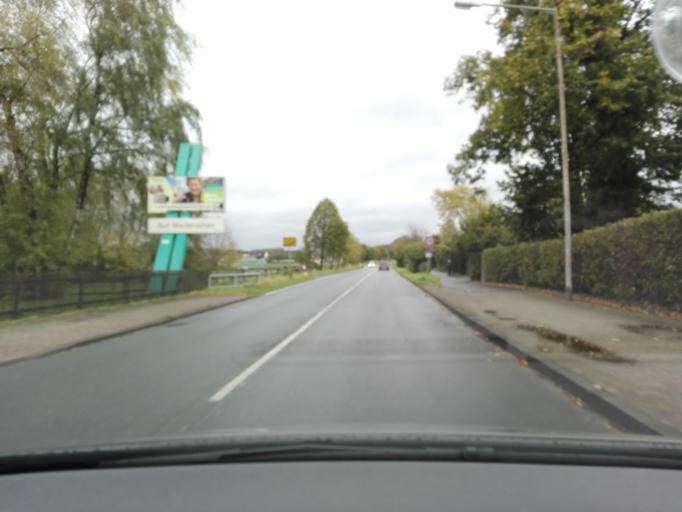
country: DE
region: North Rhine-Westphalia
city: Lunen
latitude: 51.6288
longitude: 7.5109
